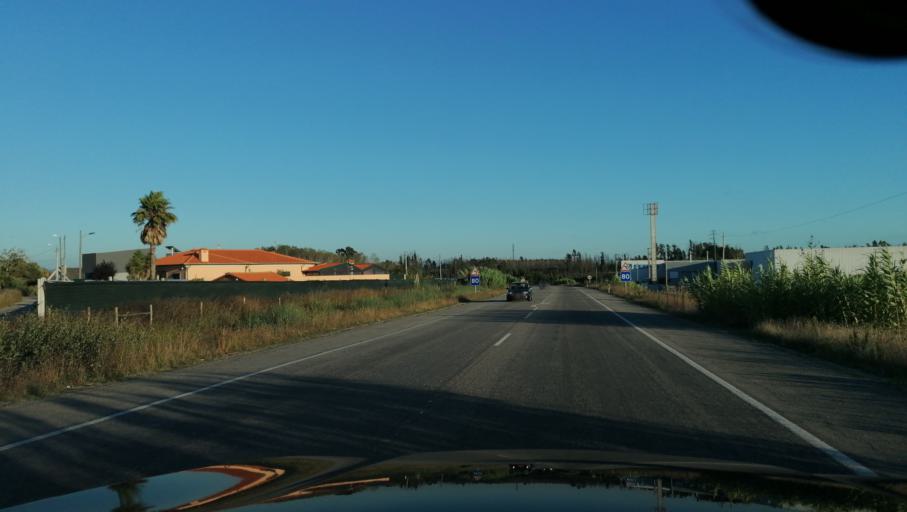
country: PT
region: Aveiro
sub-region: Aveiro
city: Oliveirinha
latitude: 40.5873
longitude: -8.6074
